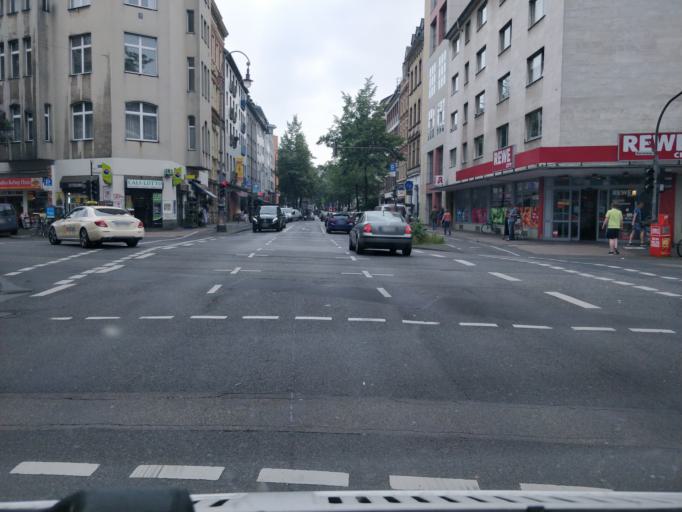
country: DE
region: North Rhine-Westphalia
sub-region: Regierungsbezirk Koln
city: Neustadt/Nord
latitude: 50.9419
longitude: 6.9361
